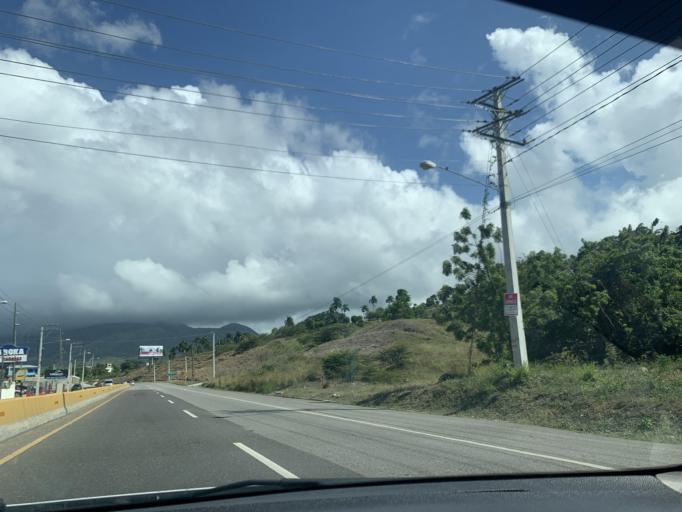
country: DO
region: Puerto Plata
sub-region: Puerto Plata
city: Puerto Plata
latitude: 19.8090
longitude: -70.7299
